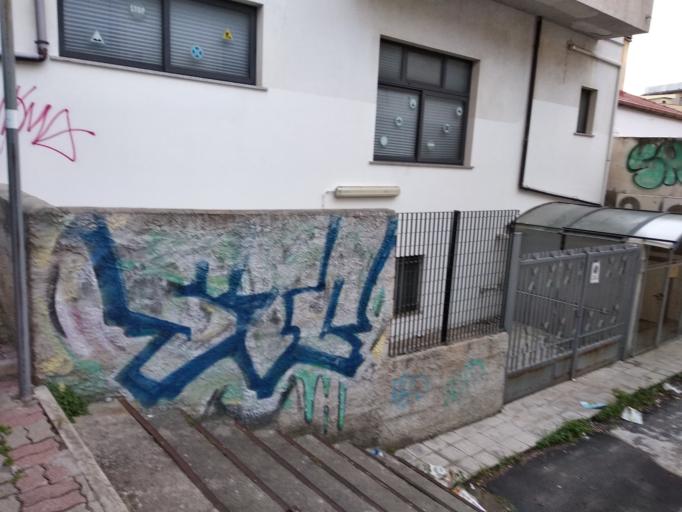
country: IT
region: Calabria
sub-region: Provincia di Catanzaro
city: Roccelletta
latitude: 38.8257
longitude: 16.6211
